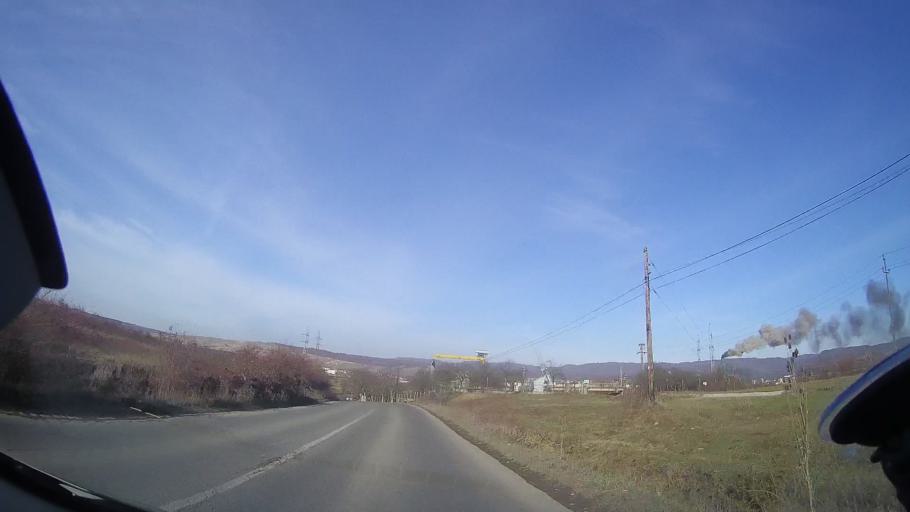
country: RO
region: Bihor
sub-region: Comuna Astileu
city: Astileu
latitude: 47.0408
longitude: 22.3914
